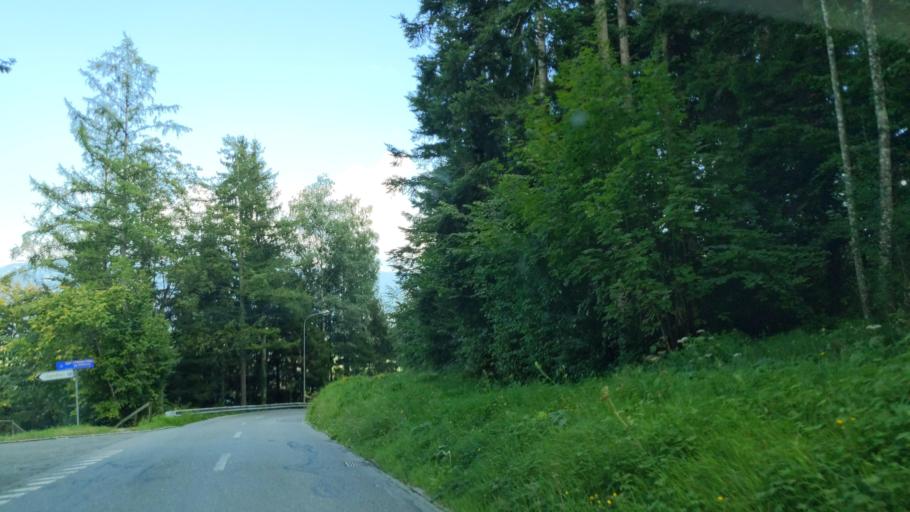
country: CH
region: Saint Gallen
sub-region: Wahlkreis Rheintal
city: Eichberg
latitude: 47.3426
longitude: 9.5132
